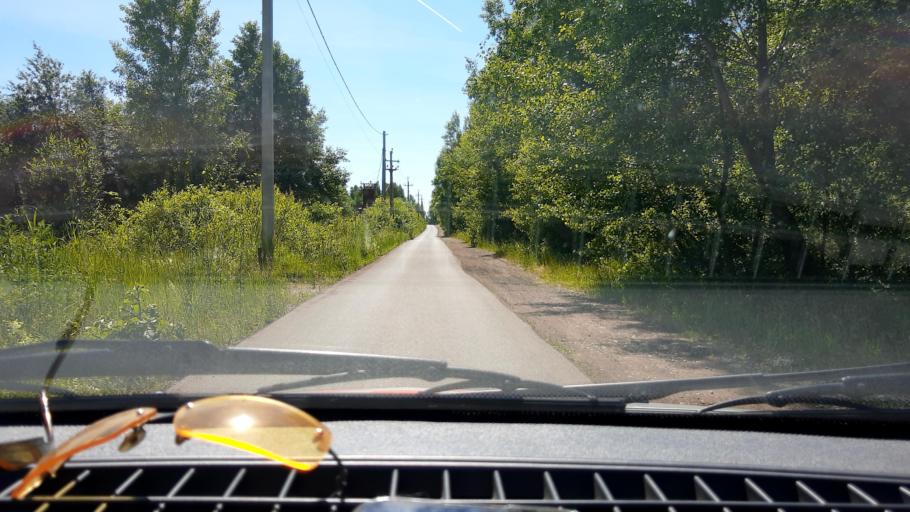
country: RU
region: Bashkortostan
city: Blagoveshchensk
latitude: 54.9715
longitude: 55.8187
